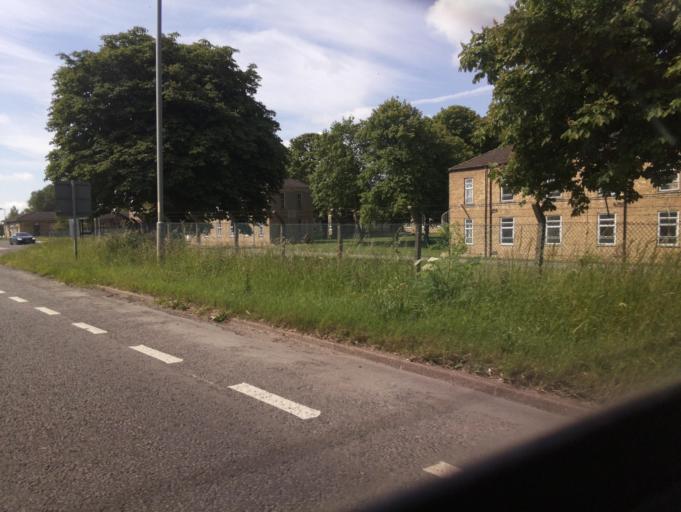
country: GB
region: England
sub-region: Lincolnshire
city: Burton
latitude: 53.3016
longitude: -0.5416
